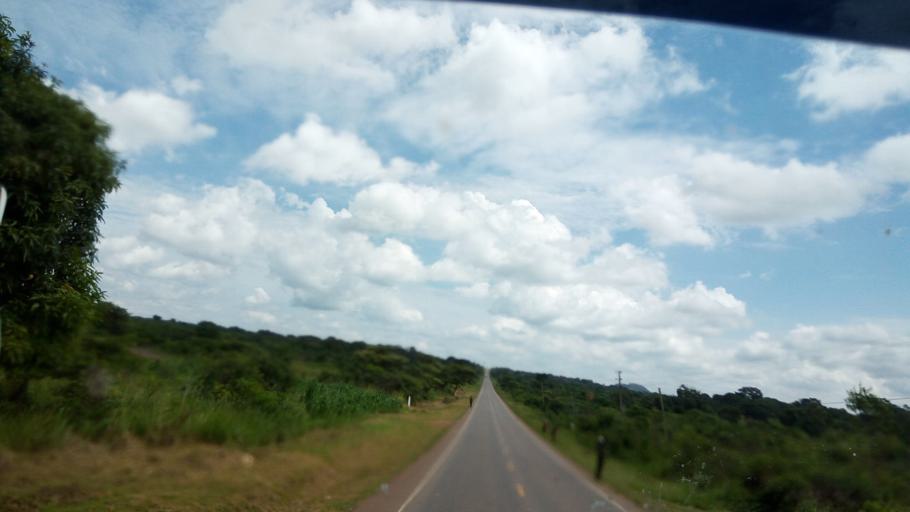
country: UG
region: Central Region
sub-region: Nakasongola District
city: Nakasongola
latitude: 1.2659
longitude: 32.4471
